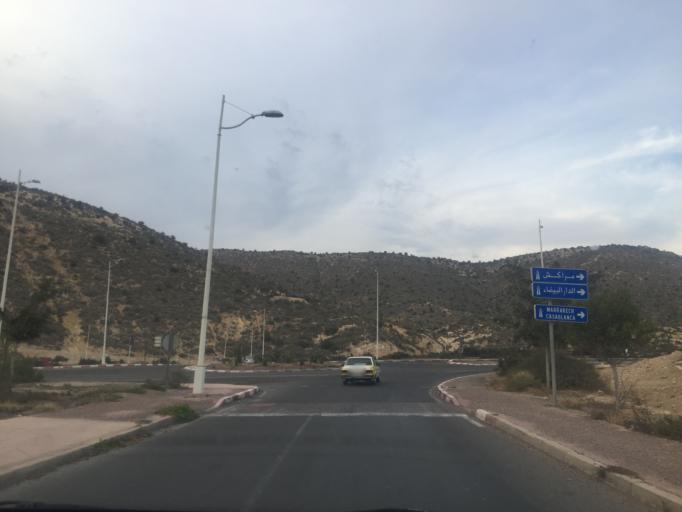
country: MA
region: Souss-Massa-Draa
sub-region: Agadir-Ida-ou-Tnan
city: Agadir
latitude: 30.4289
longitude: -9.6152
